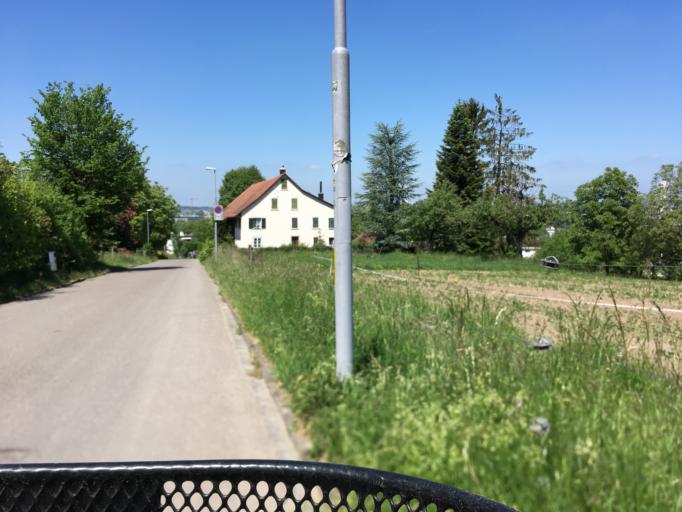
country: CH
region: Zurich
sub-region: Bezirk Zuerich
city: Zuerich (Kreis 12)
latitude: 47.4005
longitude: 8.5722
